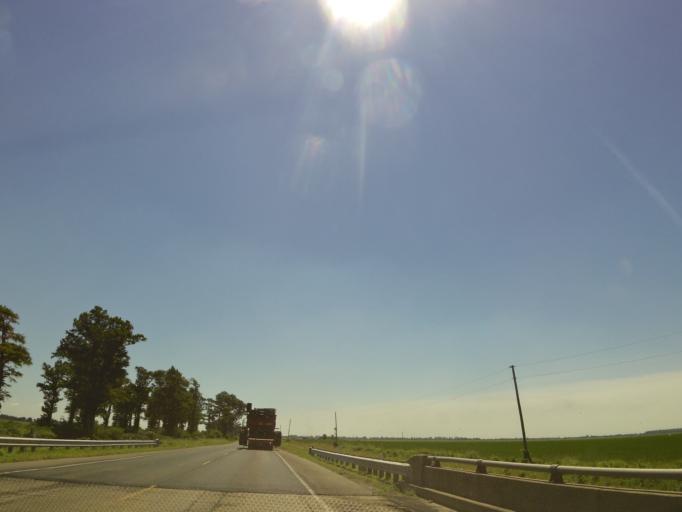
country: US
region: Missouri
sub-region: New Madrid County
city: Lilbourn
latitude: 36.5537
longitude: -89.7193
